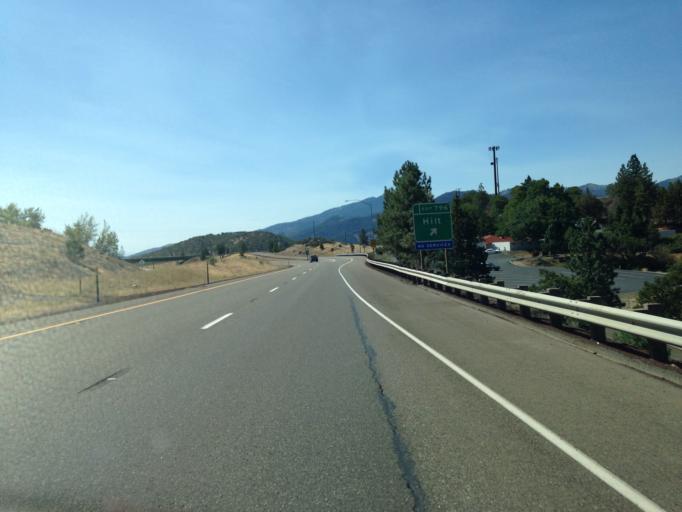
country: US
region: Oregon
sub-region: Jackson County
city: Ashland
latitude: 41.9967
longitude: -122.6104
